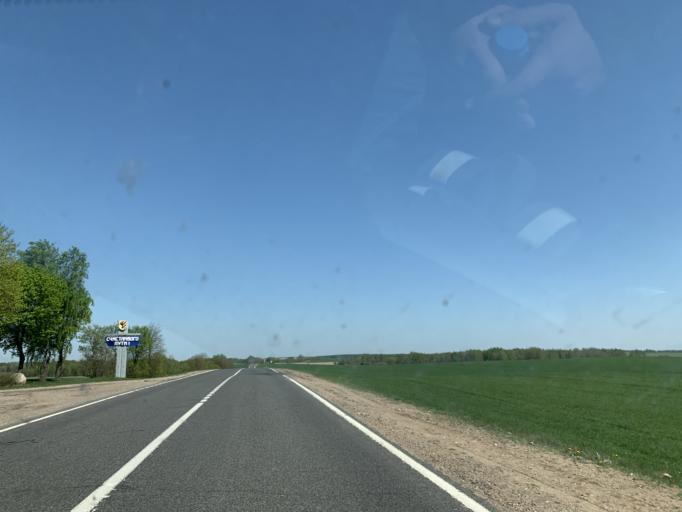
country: BY
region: Minsk
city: Nyasvizh
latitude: 53.2430
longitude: 26.8646
